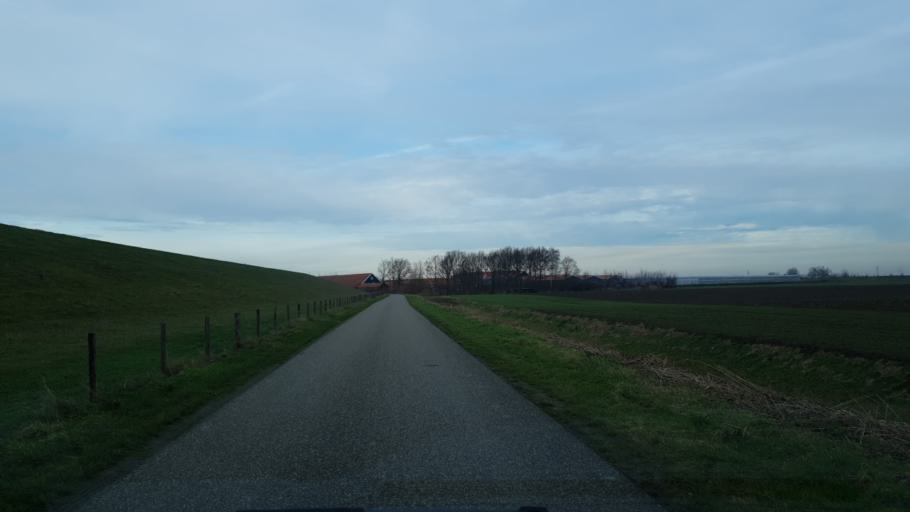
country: NL
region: Zeeland
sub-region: Gemeente Reimerswaal
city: Yerseke
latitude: 51.3976
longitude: 4.1384
